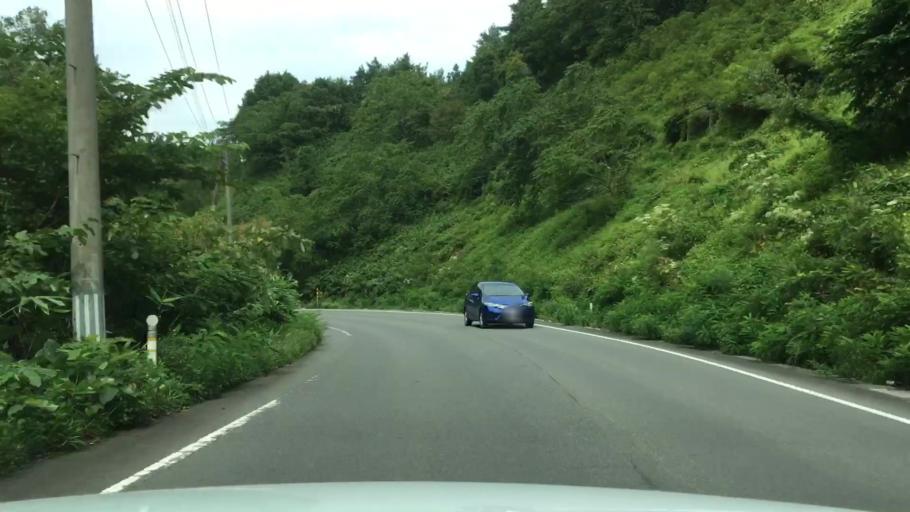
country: JP
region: Aomori
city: Shimokizukuri
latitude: 40.7287
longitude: 140.2535
